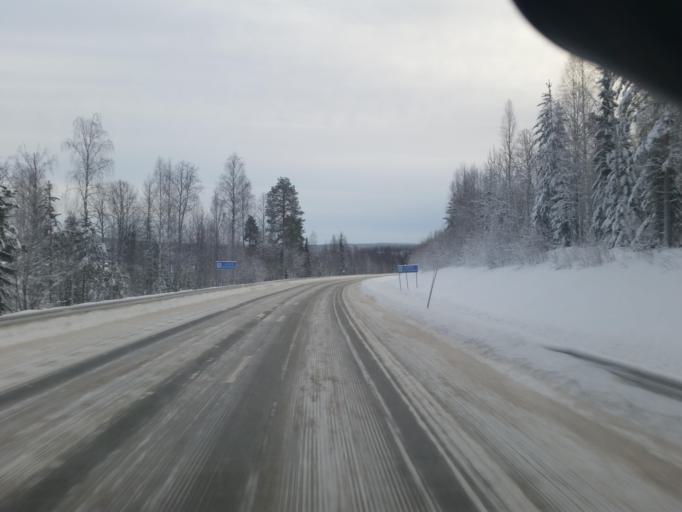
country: SE
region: Norrbotten
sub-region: Pitea Kommun
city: Norrfjarden
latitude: 65.6331
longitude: 21.3810
